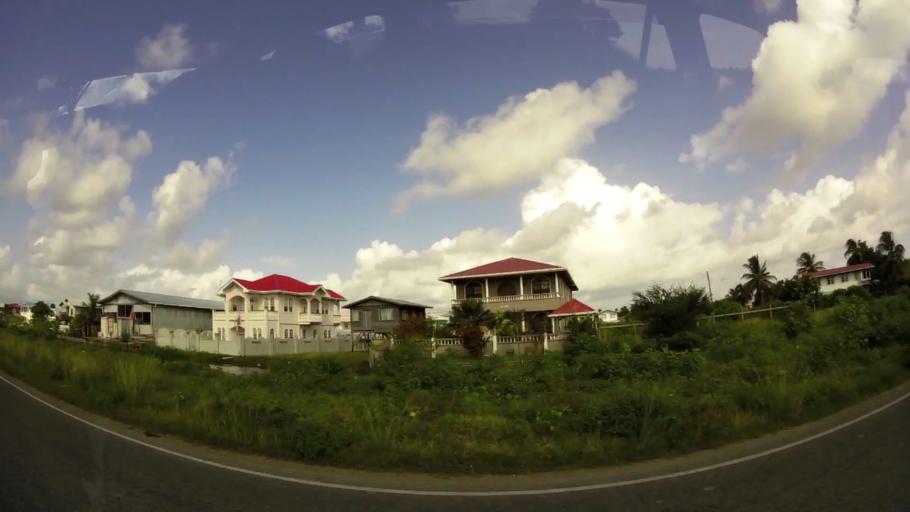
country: GY
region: Demerara-Mahaica
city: Mahaica Village
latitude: 6.7448
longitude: -57.9555
